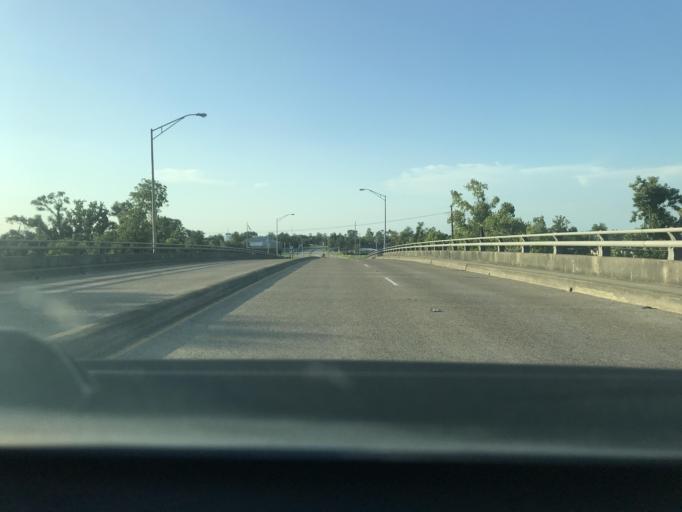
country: US
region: Louisiana
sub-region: Calcasieu Parish
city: Lake Charles
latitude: 30.2388
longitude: -93.2043
